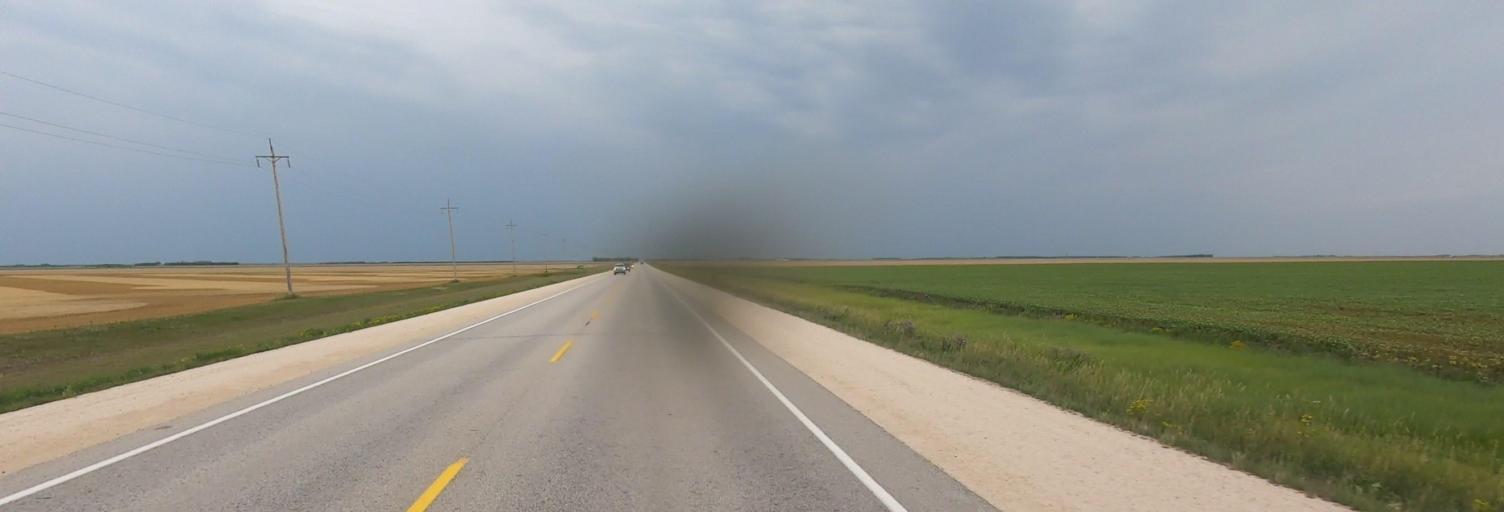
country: CA
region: Manitoba
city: Headingley
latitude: 49.7681
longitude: -97.3975
